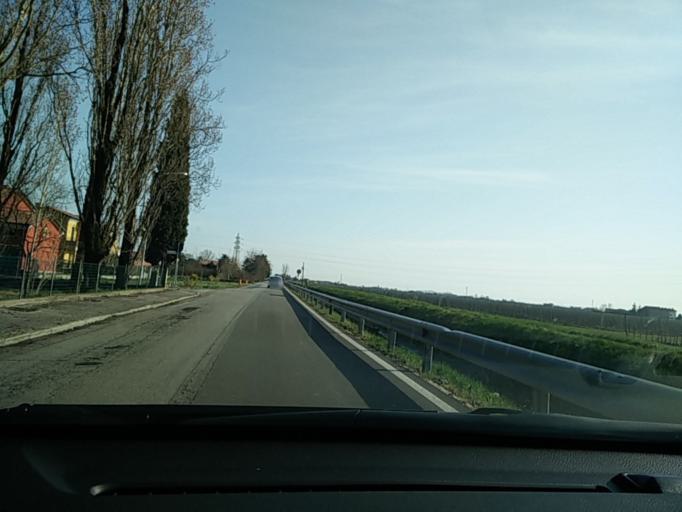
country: IT
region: Veneto
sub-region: Provincia di Venezia
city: Musile di Piave
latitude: 45.6182
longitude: 12.5292
